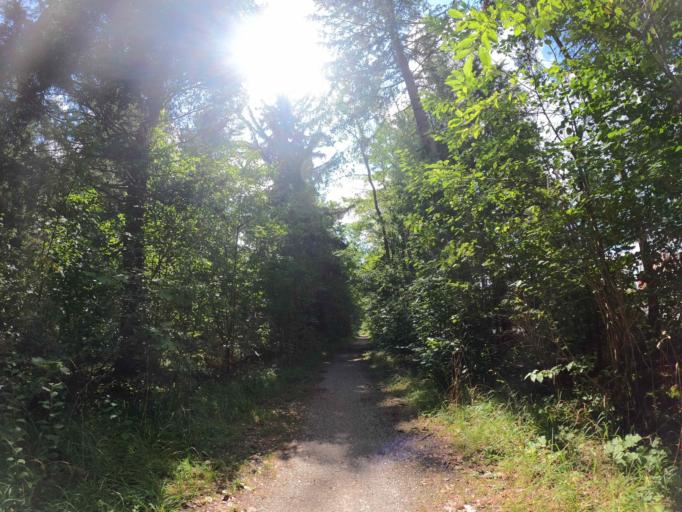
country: DE
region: Bavaria
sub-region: Upper Bavaria
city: Ottobrunn
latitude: 48.0429
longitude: 11.6657
